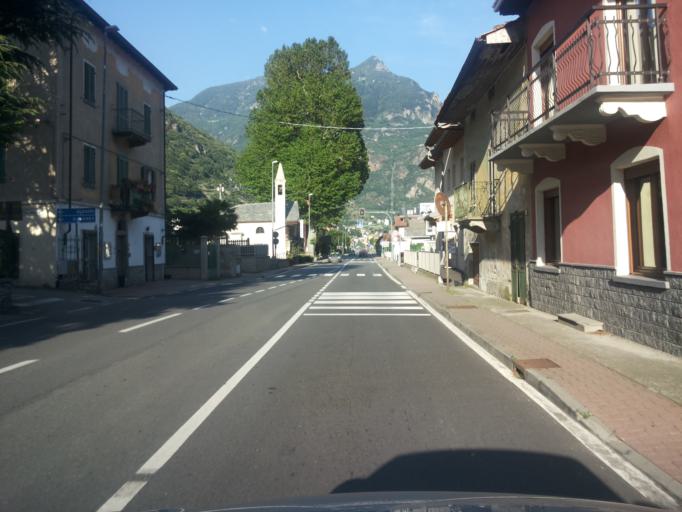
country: IT
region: Aosta Valley
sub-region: Valle d'Aosta
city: Donnas
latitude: 45.6030
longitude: 7.7720
